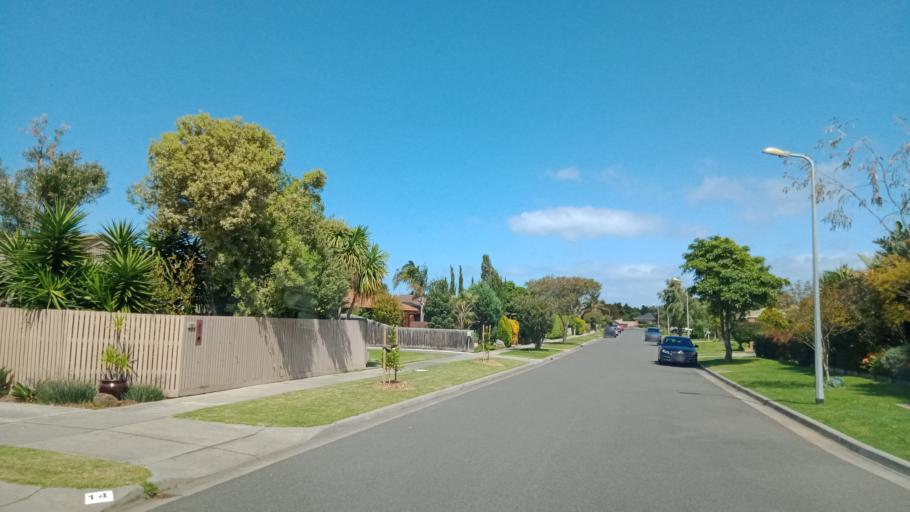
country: AU
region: Victoria
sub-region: Kingston
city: Chelsea Heights
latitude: -38.0405
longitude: 145.1317
